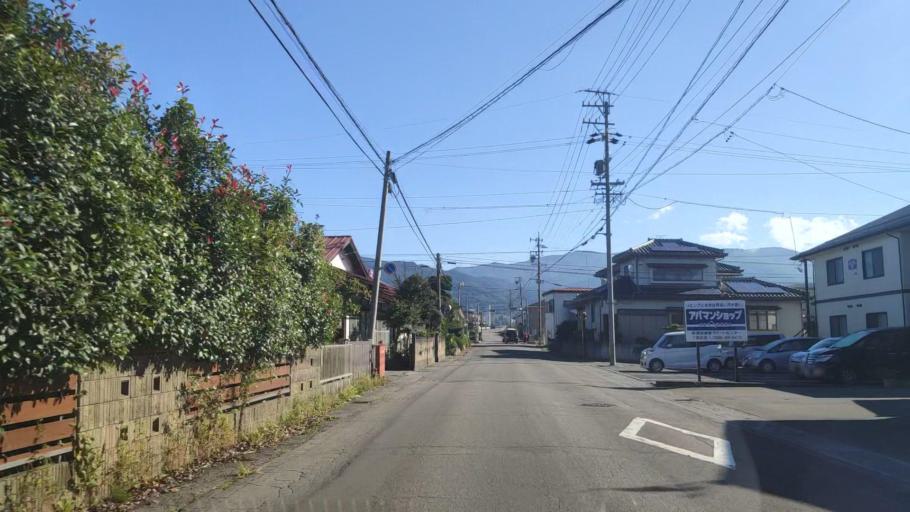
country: JP
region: Nagano
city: Okaya
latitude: 36.0640
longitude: 138.0742
